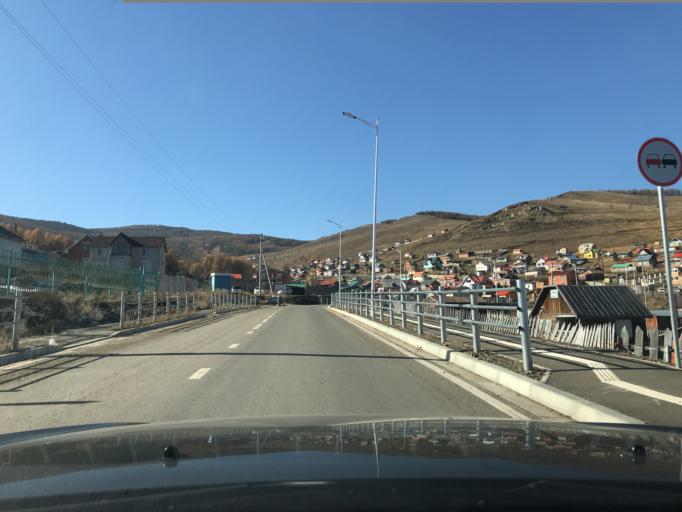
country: MN
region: Ulaanbaatar
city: Ulaanbaatar
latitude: 48.0372
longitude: 106.8997
